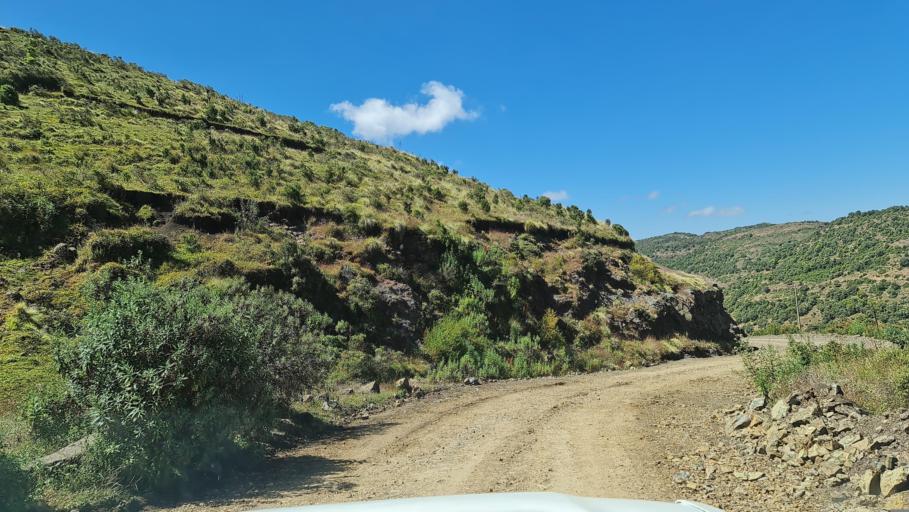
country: ET
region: Amhara
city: Debark'
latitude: 13.2326
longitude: 38.0708
